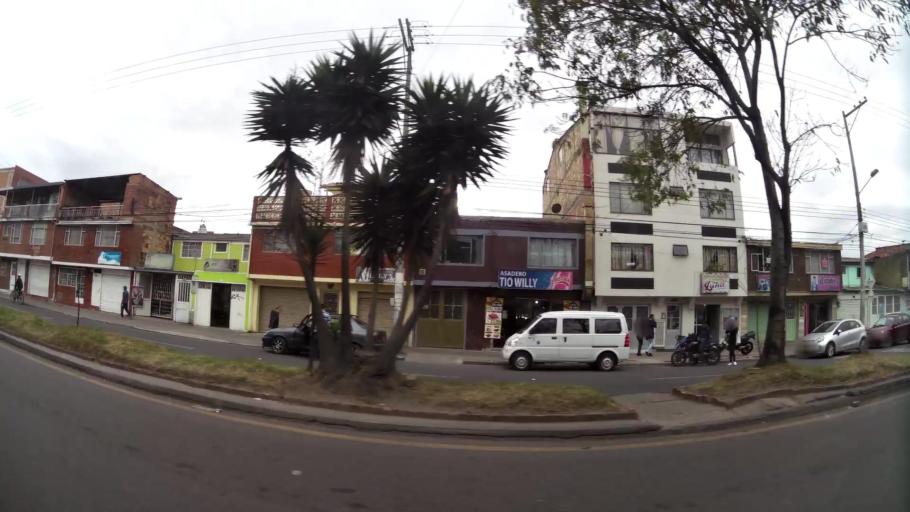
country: CO
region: Bogota D.C.
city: Bogota
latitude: 4.5897
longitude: -74.1422
